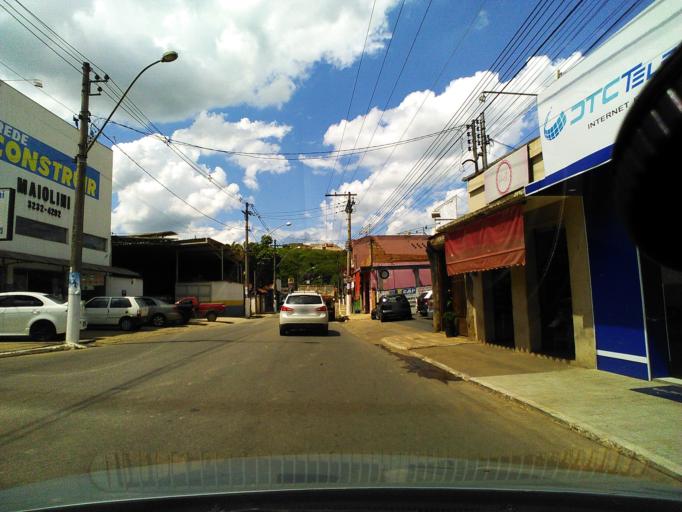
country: BR
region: Minas Gerais
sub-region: Tres Coracoes
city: Tres Coracoes
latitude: -21.7116
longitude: -45.2635
